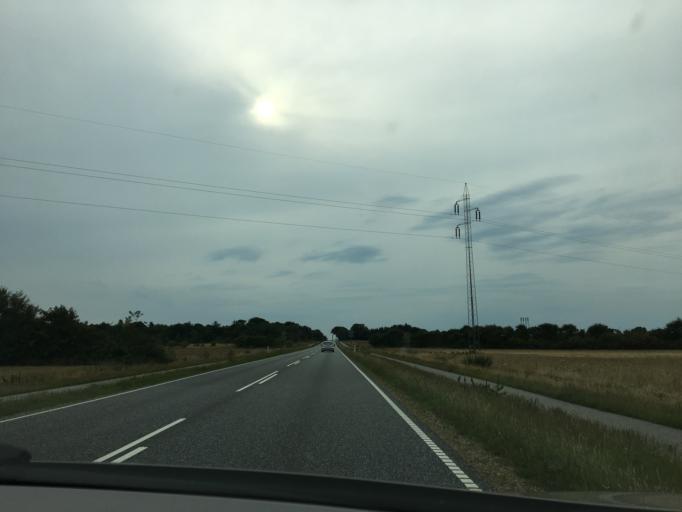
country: DK
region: Central Jutland
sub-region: Ringkobing-Skjern Kommune
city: Ringkobing
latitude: 56.0867
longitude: 8.2955
